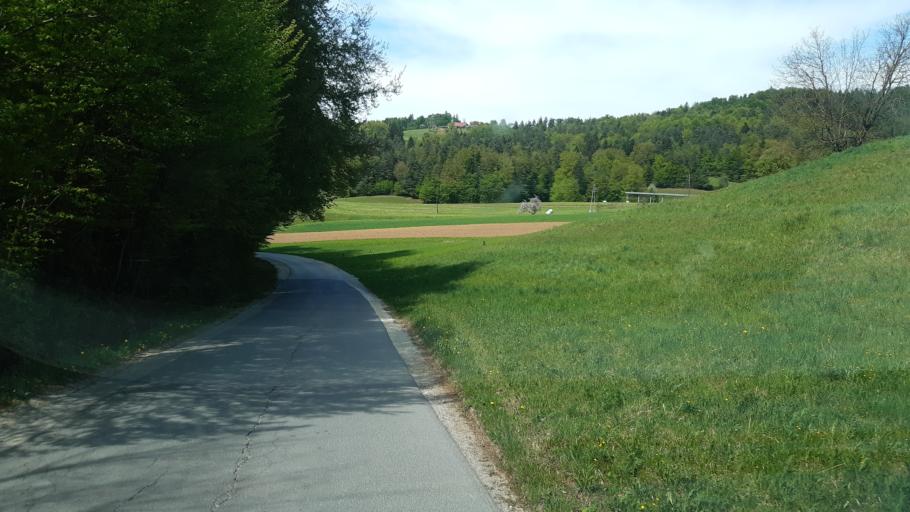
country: SI
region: Lukovica
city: Lukovica pri Domzalah
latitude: 46.1752
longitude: 14.6667
